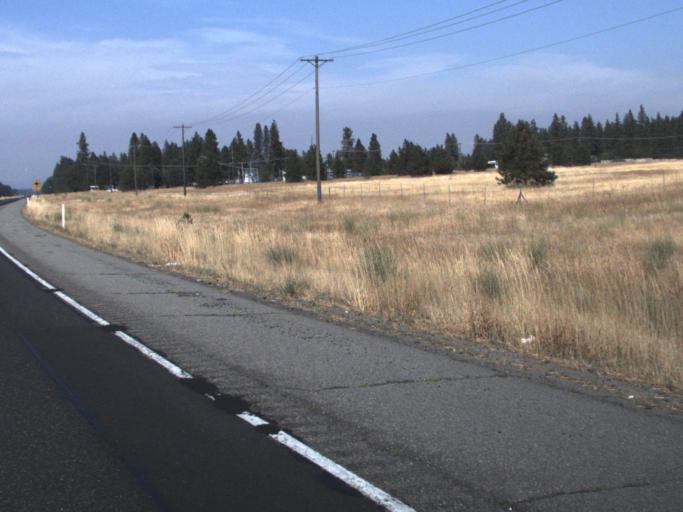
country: US
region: Washington
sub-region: Spokane County
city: Mead
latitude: 47.8341
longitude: -117.3534
